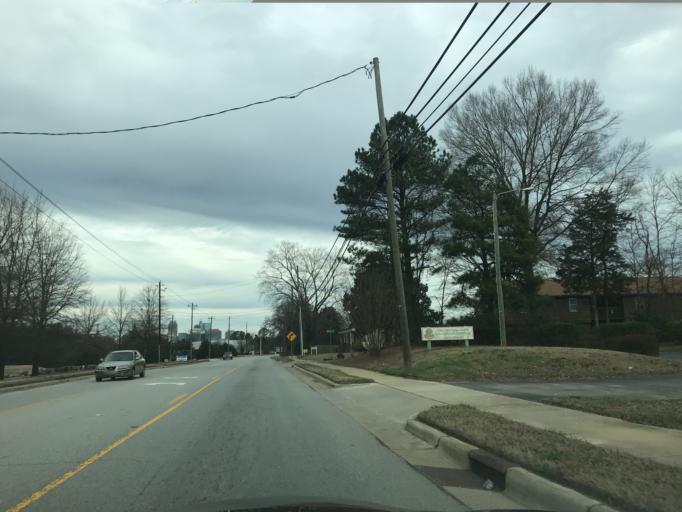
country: US
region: North Carolina
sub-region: Wake County
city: Raleigh
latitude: 35.7468
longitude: -78.6315
